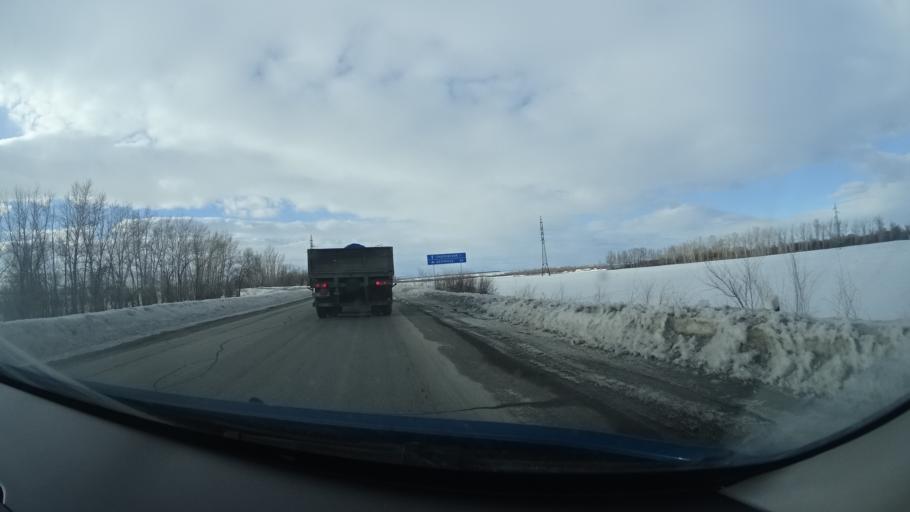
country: RU
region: Chelyabinsk
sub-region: Gorod Magnitogorsk
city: Magnitogorsk
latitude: 53.5840
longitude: 58.8838
